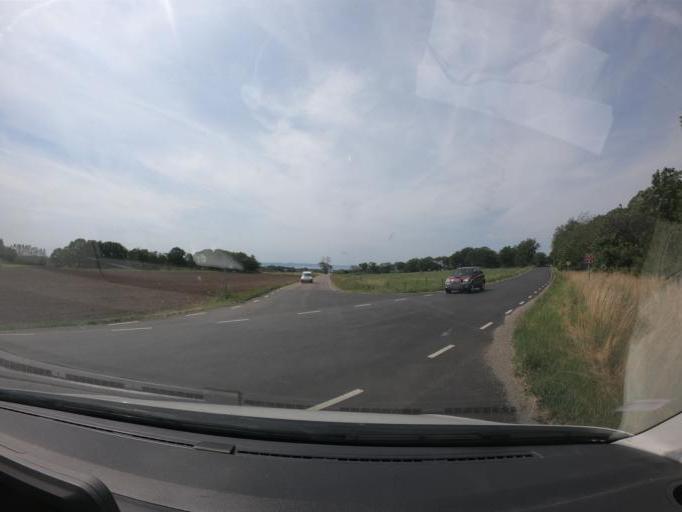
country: SE
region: Skane
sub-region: Angelholms Kommun
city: Vejbystrand
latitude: 56.3891
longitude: 12.7156
